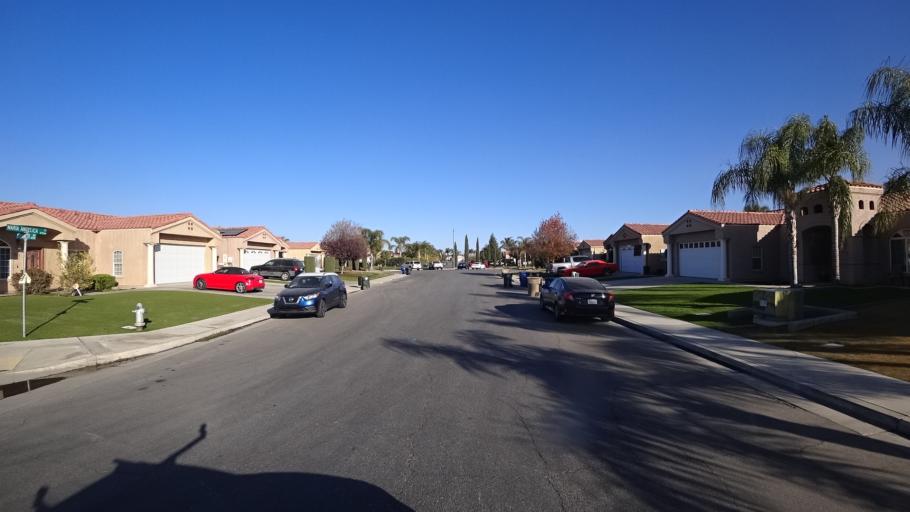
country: US
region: California
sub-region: Kern County
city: Greenfield
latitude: 35.2755
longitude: -119.0322
